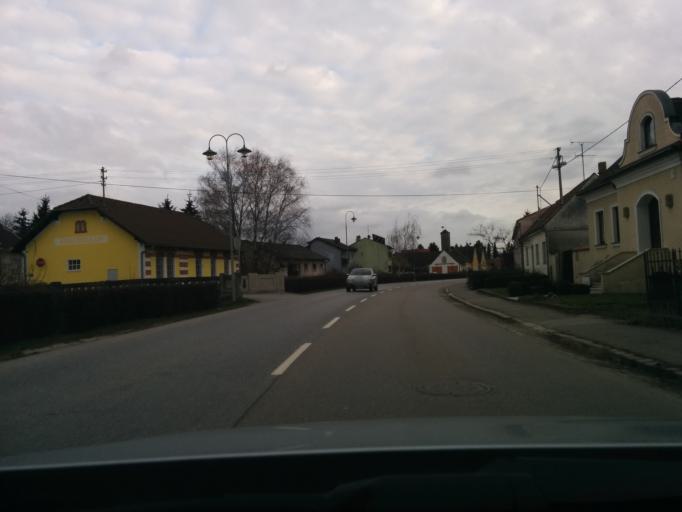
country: AT
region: Lower Austria
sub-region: Politischer Bezirk Mistelbach
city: Asparn an der Zaya
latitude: 48.6101
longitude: 16.5391
